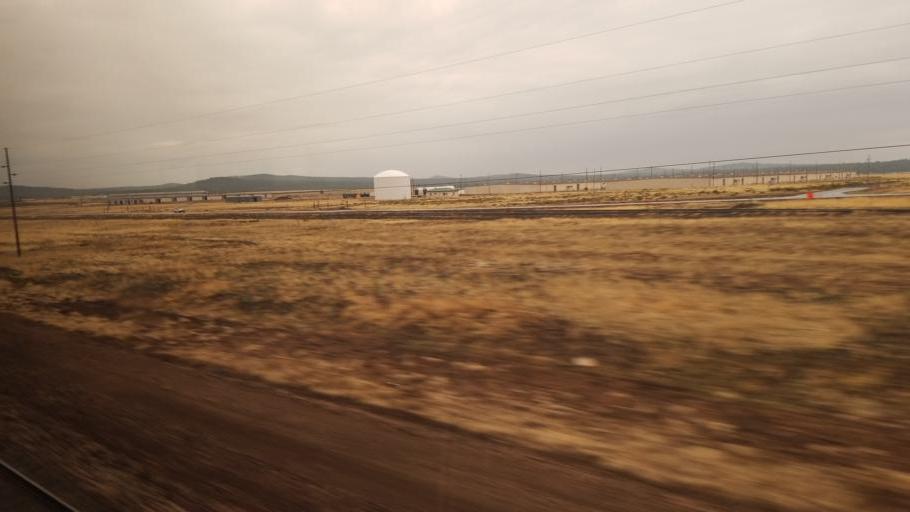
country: US
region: Arizona
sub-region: Coconino County
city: Parks
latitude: 35.2383
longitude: -111.8424
